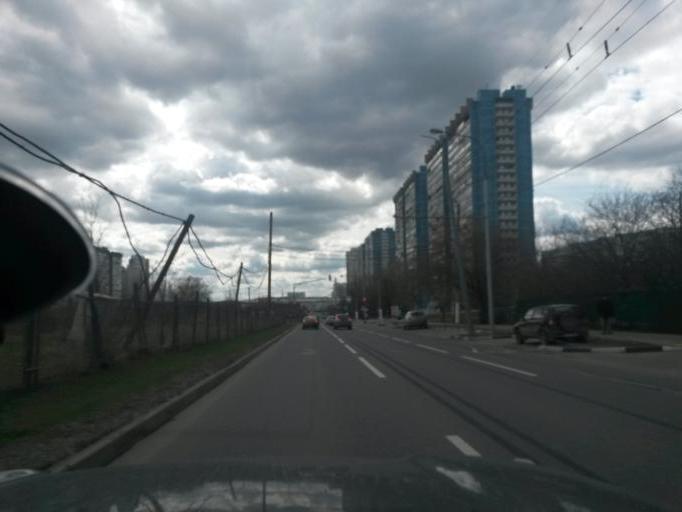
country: RU
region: Moscow
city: Yasenevo
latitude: 55.6044
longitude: 37.5312
